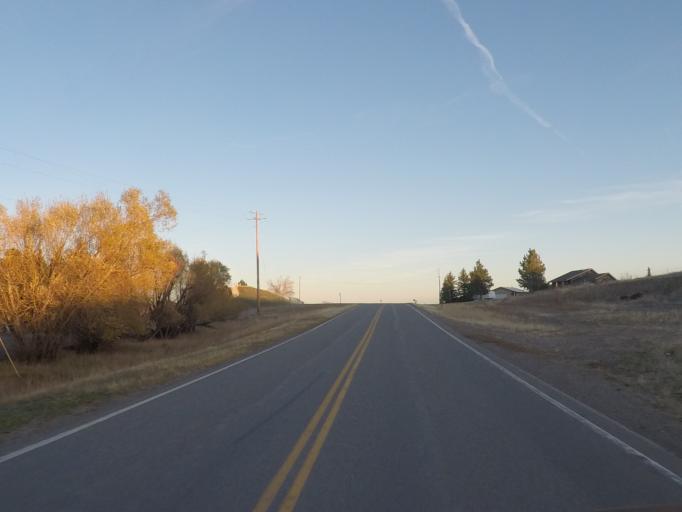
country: US
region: Montana
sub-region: Sweet Grass County
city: Big Timber
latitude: 45.7730
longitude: -109.7999
